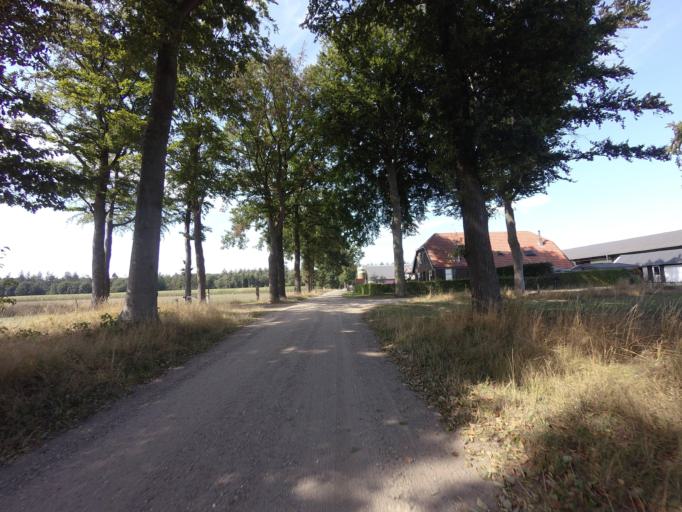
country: NL
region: Gelderland
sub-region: Gemeente Apeldoorn
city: Loenen
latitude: 52.1368
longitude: 6.0311
